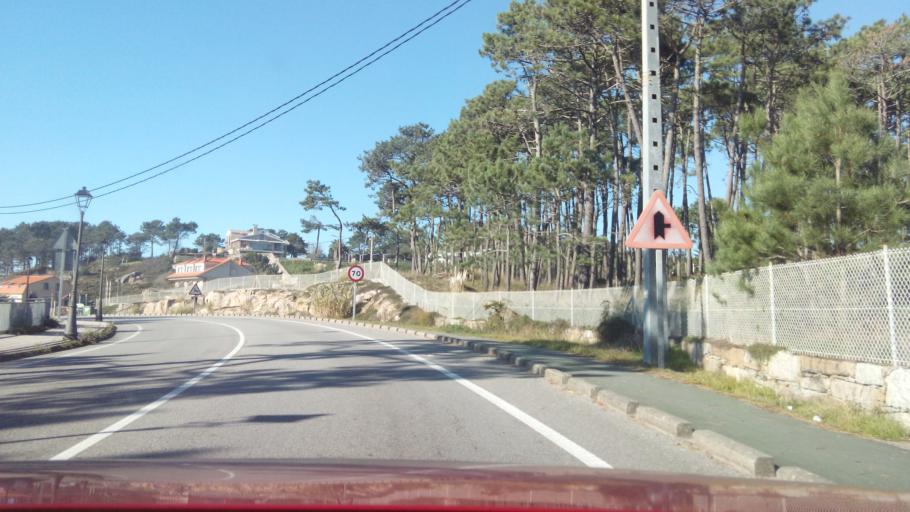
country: ES
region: Galicia
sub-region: Provincia de Pontevedra
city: O Grove
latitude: 42.4583
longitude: -8.8856
